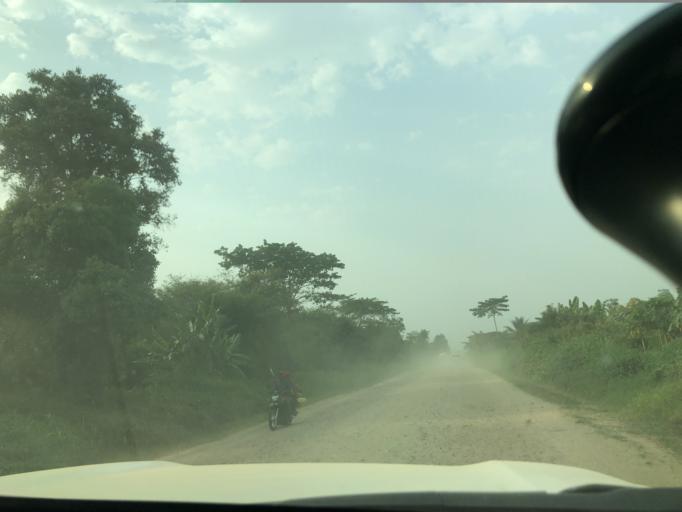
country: UG
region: Western Region
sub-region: Kasese District
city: Margherita
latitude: 0.2705
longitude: 29.6745
